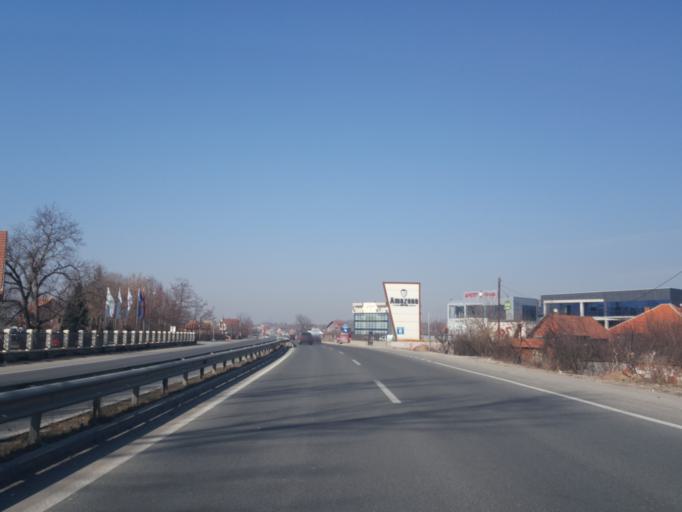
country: XK
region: Pristina
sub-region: Komuna e Obiliqit
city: Obiliq
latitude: 42.7334
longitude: 21.0703
